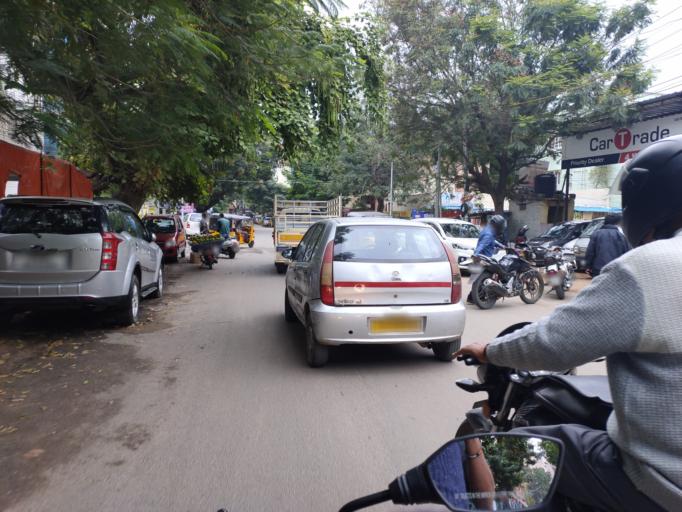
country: IN
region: Telangana
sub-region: Rangareddi
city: Kukatpalli
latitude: 17.4478
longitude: 78.4473
